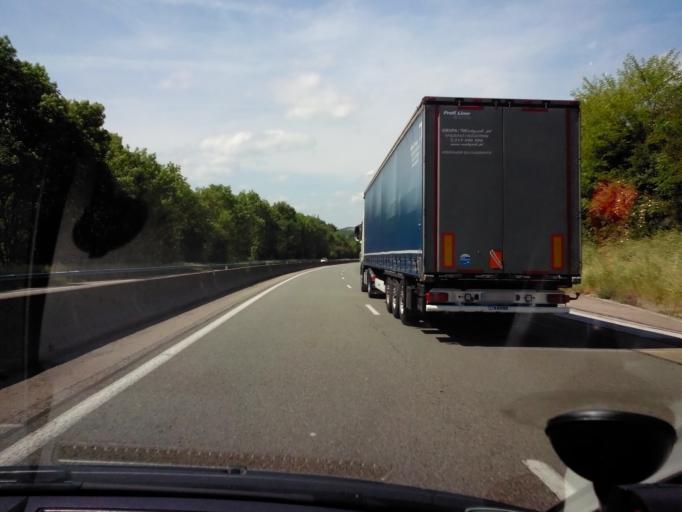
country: FR
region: Champagne-Ardenne
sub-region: Departement de la Haute-Marne
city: Avrecourt
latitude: 47.9611
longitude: 5.4639
